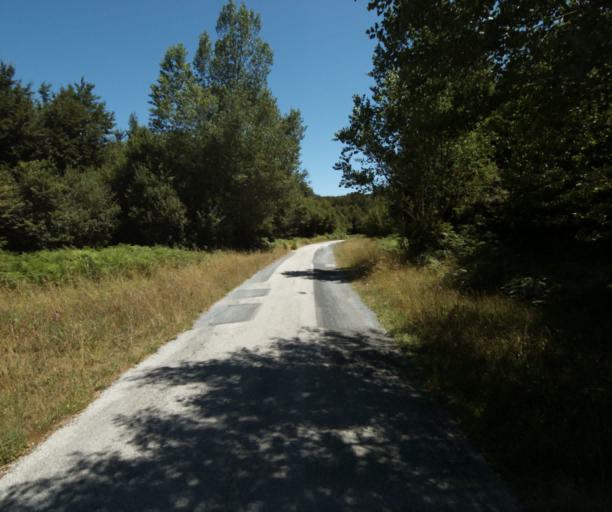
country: FR
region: Midi-Pyrenees
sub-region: Departement du Tarn
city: Dourgne
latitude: 43.4096
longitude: 2.1964
